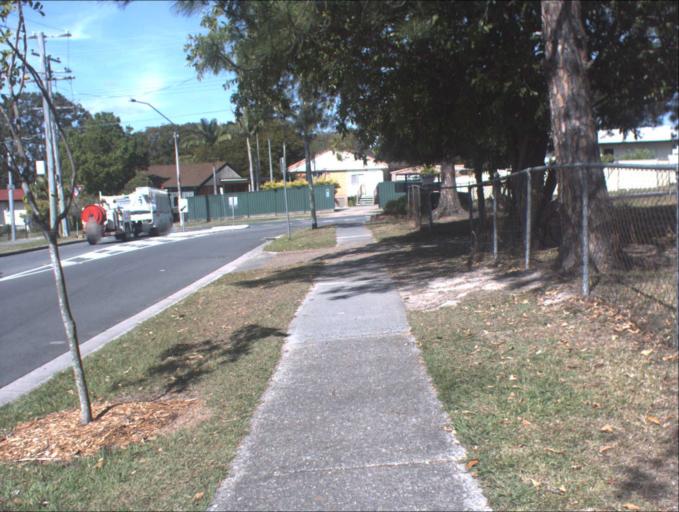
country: AU
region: Queensland
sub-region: Logan
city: Logan City
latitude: -27.6354
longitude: 153.1079
